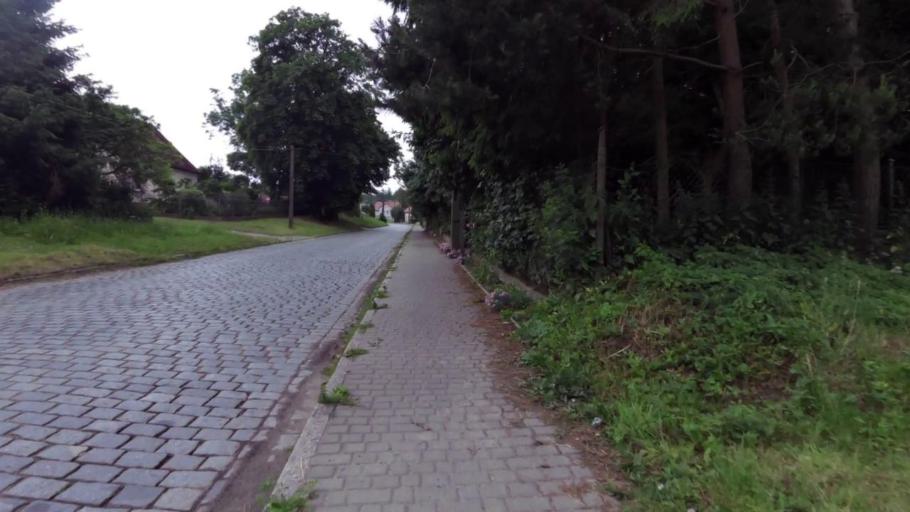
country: PL
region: West Pomeranian Voivodeship
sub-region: Powiat kamienski
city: Wolin
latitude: 53.8419
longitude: 14.6271
